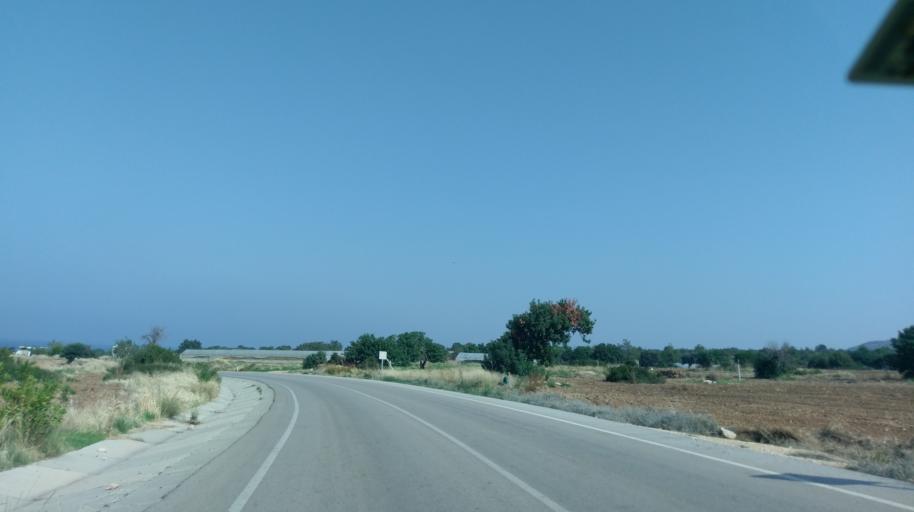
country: CY
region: Ammochostos
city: Lefkonoiko
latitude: 35.3788
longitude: 33.7192
